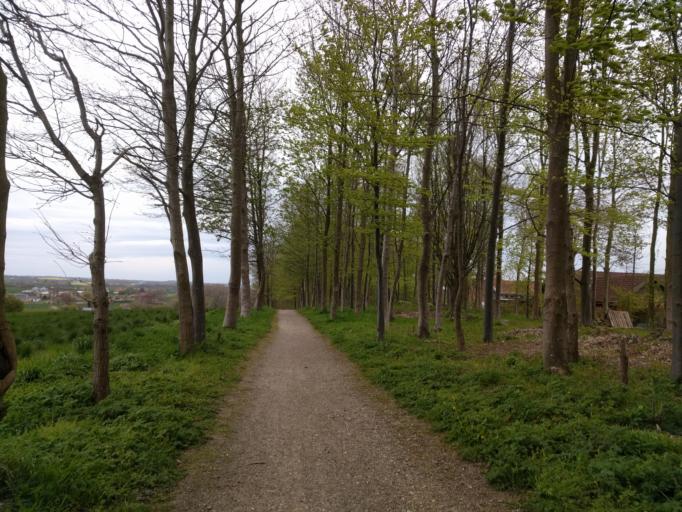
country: DK
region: South Denmark
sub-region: Kerteminde Kommune
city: Munkebo
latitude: 55.4676
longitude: 10.5769
